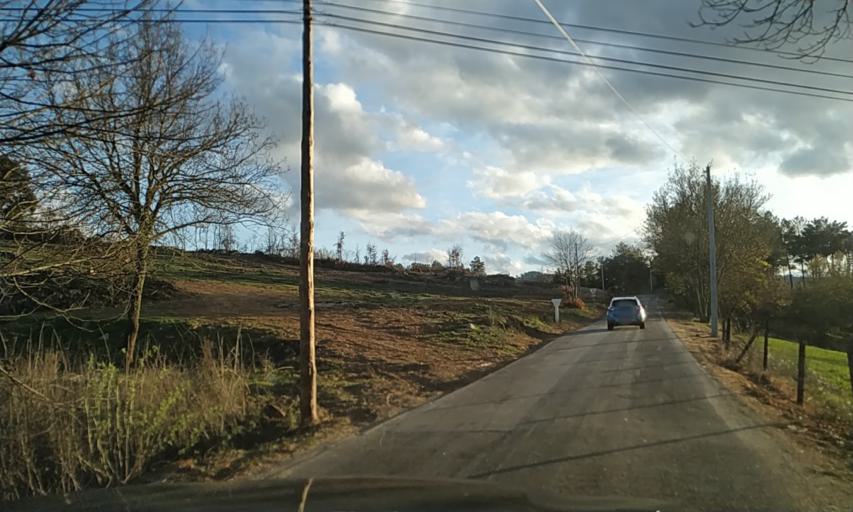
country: PT
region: Braganca
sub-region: Carrazeda de Ansiaes
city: Carrazeda de Anciaes
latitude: 41.2308
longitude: -7.3388
